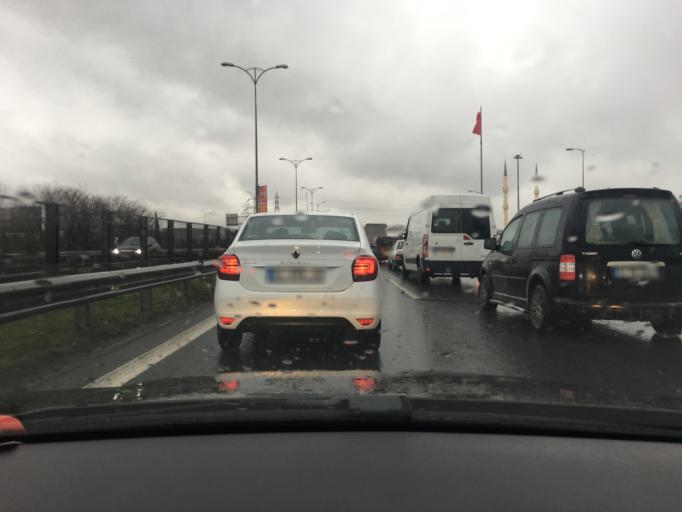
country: TR
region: Istanbul
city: Esenler
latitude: 41.0478
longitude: 28.8850
